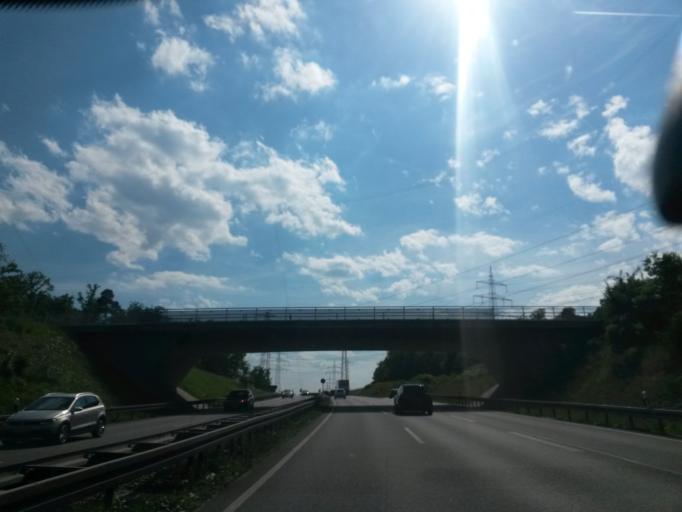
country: DE
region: Baden-Wuerttemberg
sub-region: Regierungsbezirk Stuttgart
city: Renningen
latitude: 48.7815
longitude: 8.9724
